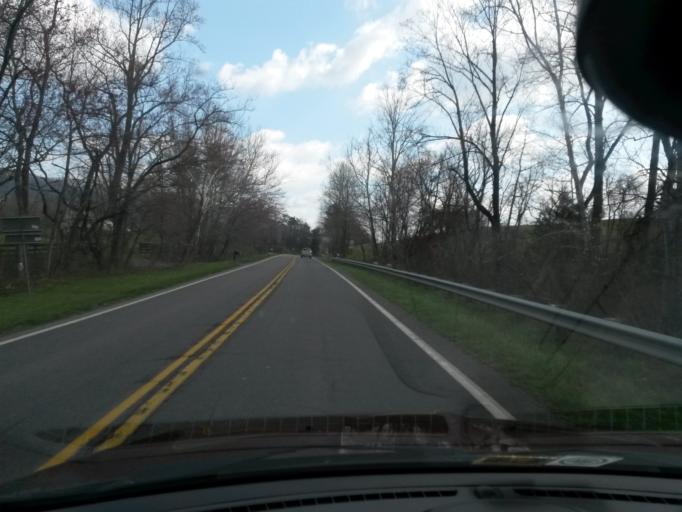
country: US
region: Virginia
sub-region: City of Waynesboro
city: Waynesboro
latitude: 38.0241
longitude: -78.8149
